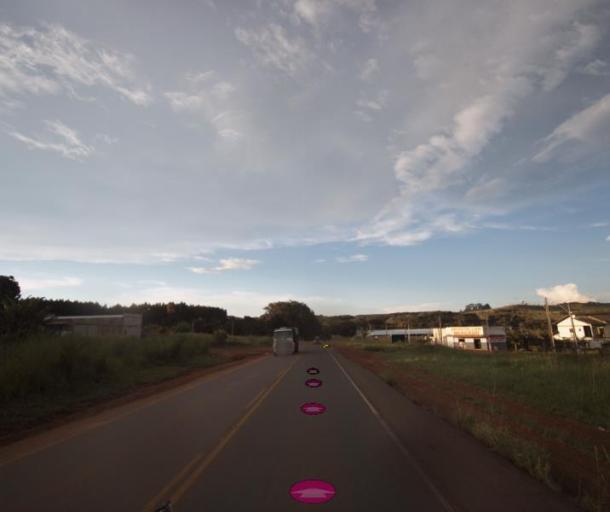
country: BR
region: Goias
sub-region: Anapolis
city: Anapolis
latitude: -16.2510
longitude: -48.9352
